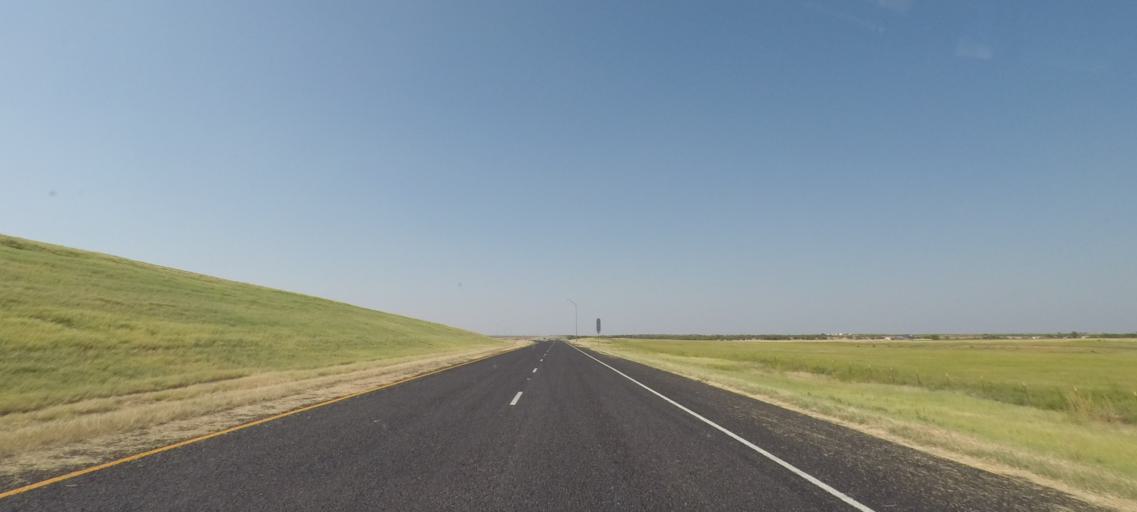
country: US
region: Texas
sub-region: Baylor County
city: Seymour
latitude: 33.5964
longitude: -99.2407
